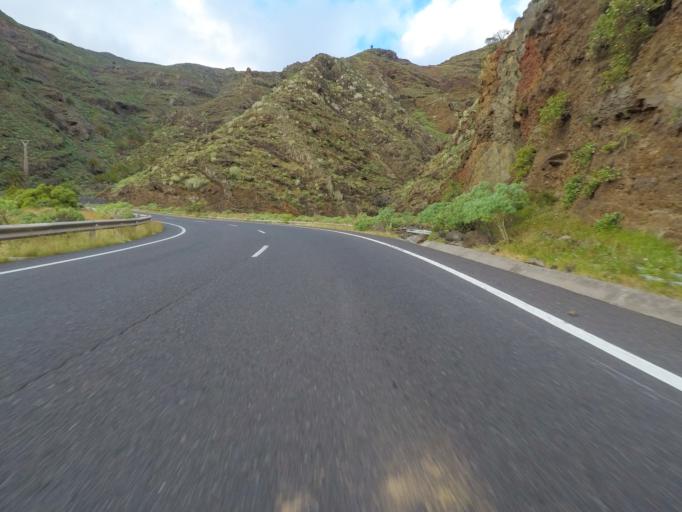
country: ES
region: Canary Islands
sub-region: Provincia de Santa Cruz de Tenerife
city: San Sebastian de la Gomera
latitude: 28.1244
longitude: -17.1469
